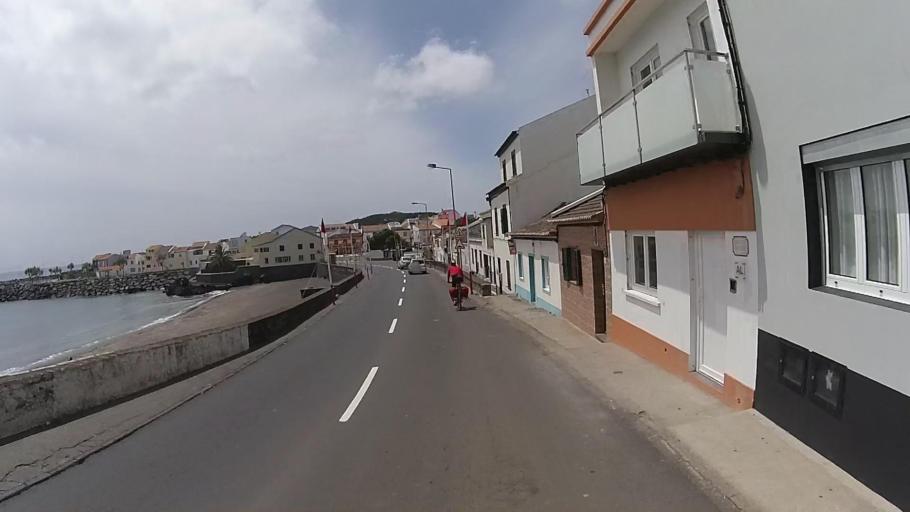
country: PT
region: Azores
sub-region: Ponta Delgada
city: Rosto de Cao
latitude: 37.7506
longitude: -25.6309
